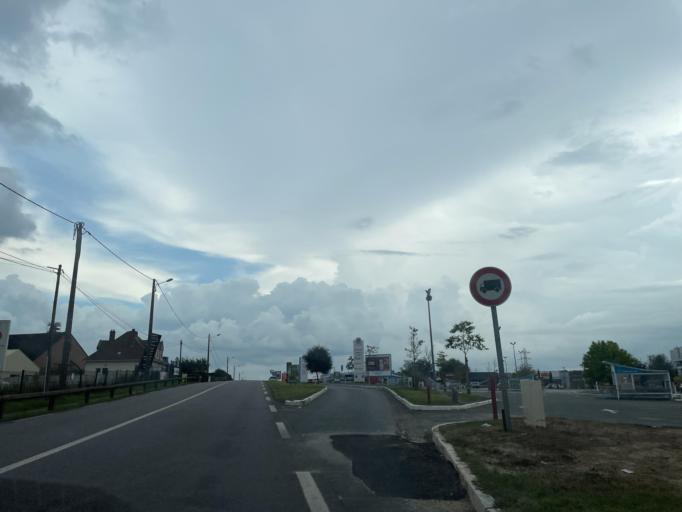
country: FR
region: Haute-Normandie
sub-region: Departement de la Seine-Maritime
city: Gournay-en-Bray
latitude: 49.4798
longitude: 1.7390
